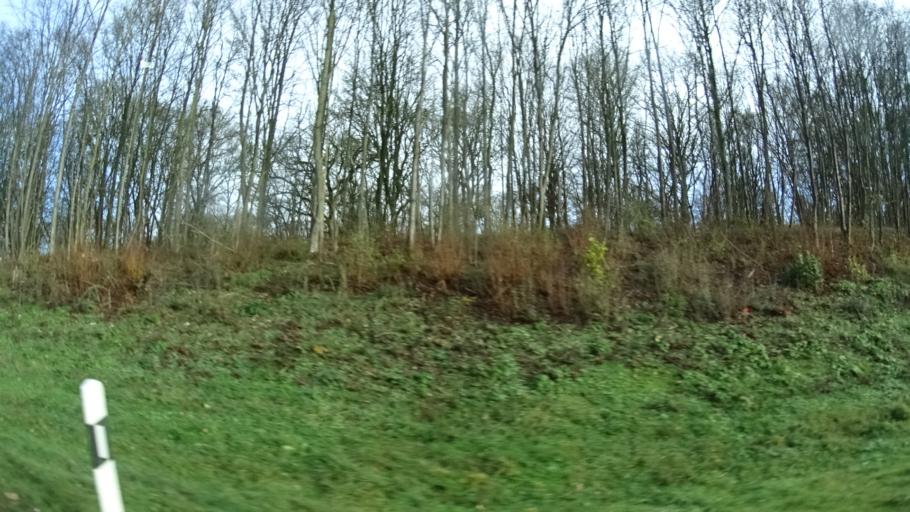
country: DE
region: Bavaria
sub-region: Regierungsbezirk Unterfranken
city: Estenfeld
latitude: 49.8538
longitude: 9.9989
